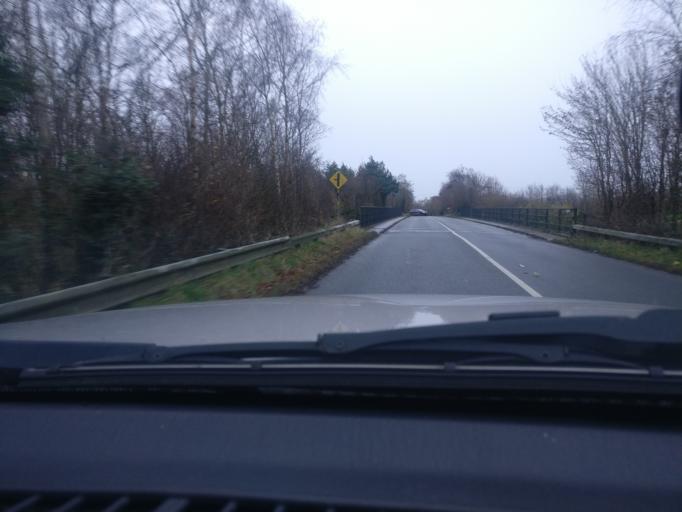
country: IE
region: Leinster
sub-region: Kildare
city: Maynooth
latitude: 53.3656
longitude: -6.5660
